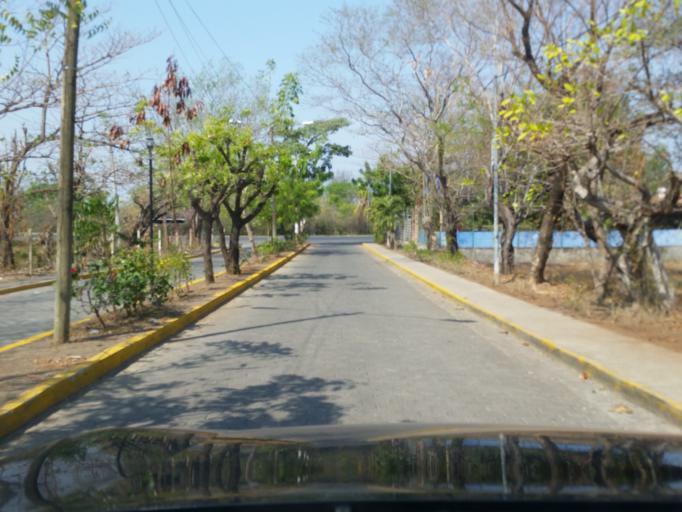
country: NI
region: Granada
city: Granada
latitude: 11.9380
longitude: -85.9760
